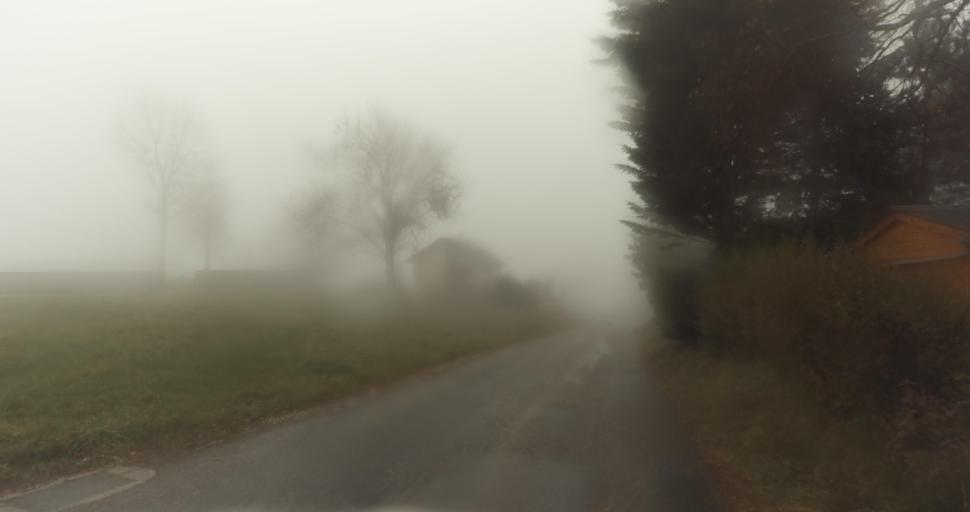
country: FR
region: Rhone-Alpes
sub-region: Departement de la Haute-Savoie
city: Thorens-Glieres
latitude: 45.9764
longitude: 6.2167
